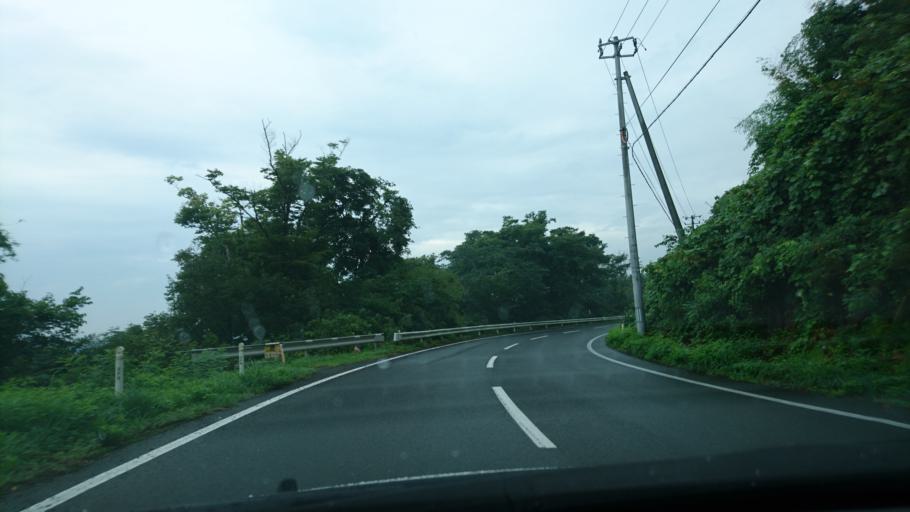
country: JP
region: Iwate
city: Ichinoseki
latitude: 38.8822
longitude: 141.2631
